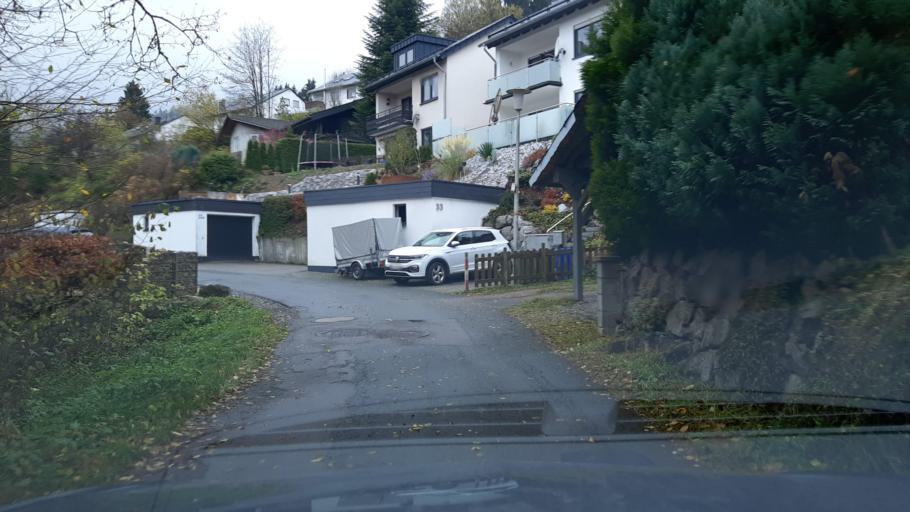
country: DE
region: Hesse
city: Willingen
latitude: 51.2867
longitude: 8.5768
